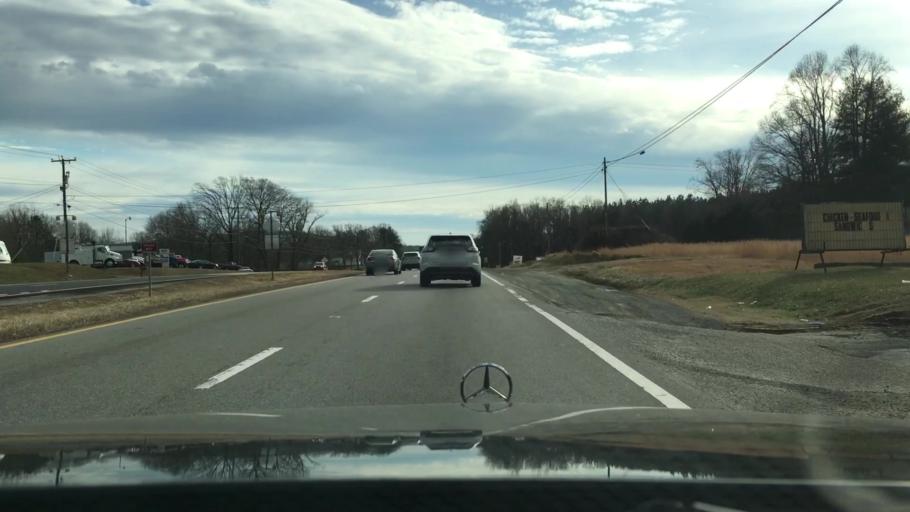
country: US
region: Virginia
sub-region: Pittsylvania County
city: Chatham
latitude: 36.7882
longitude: -79.3942
